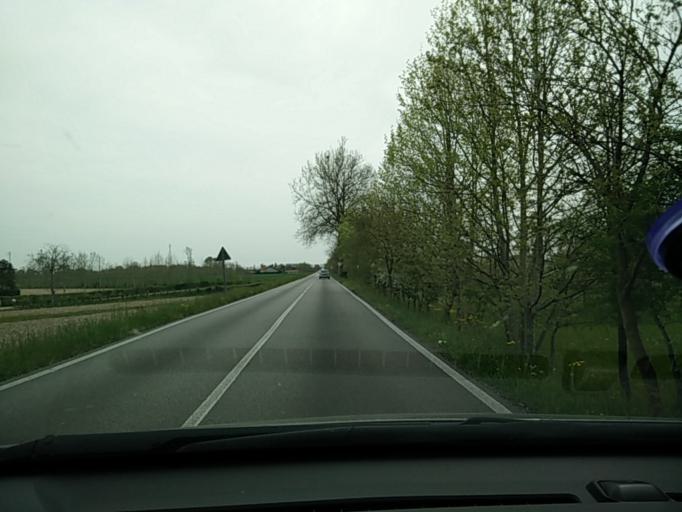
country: IT
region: Veneto
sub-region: Provincia di Venezia
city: Fossalta di Piave
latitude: 45.6411
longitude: 12.5196
